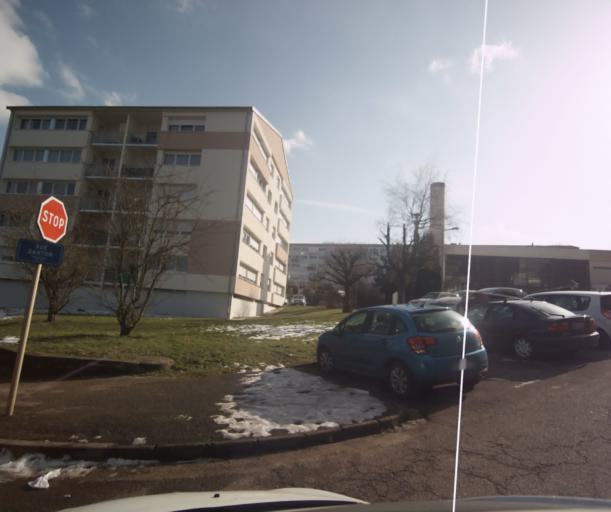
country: FR
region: Franche-Comte
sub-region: Departement du Doubs
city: Morre
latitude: 47.2451
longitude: 6.0528
